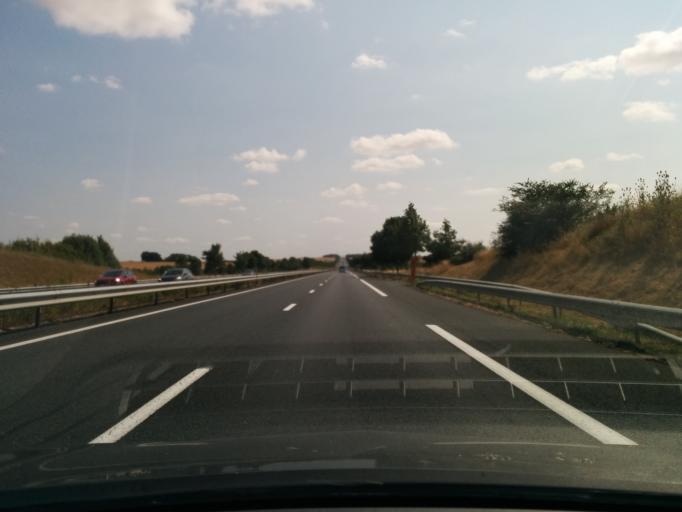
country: FR
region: Centre
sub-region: Departement de l'Indre
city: Vatan
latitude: 47.0198
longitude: 1.7856
